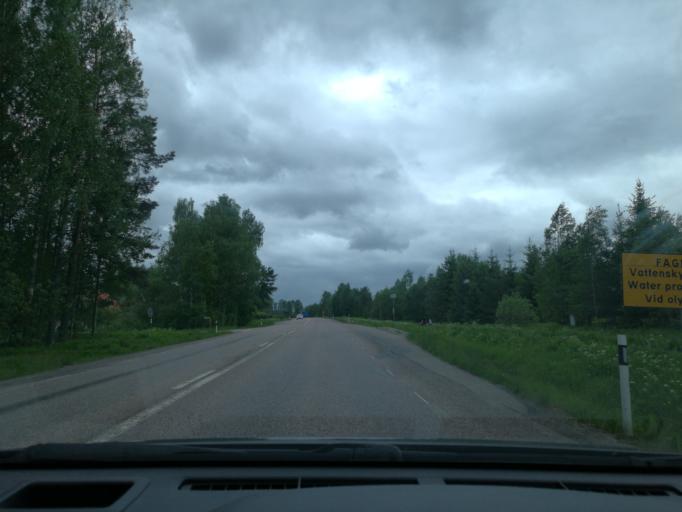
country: SE
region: Vaestmanland
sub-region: Fagersta Kommun
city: Fagersta
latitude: 59.9683
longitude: 15.7717
